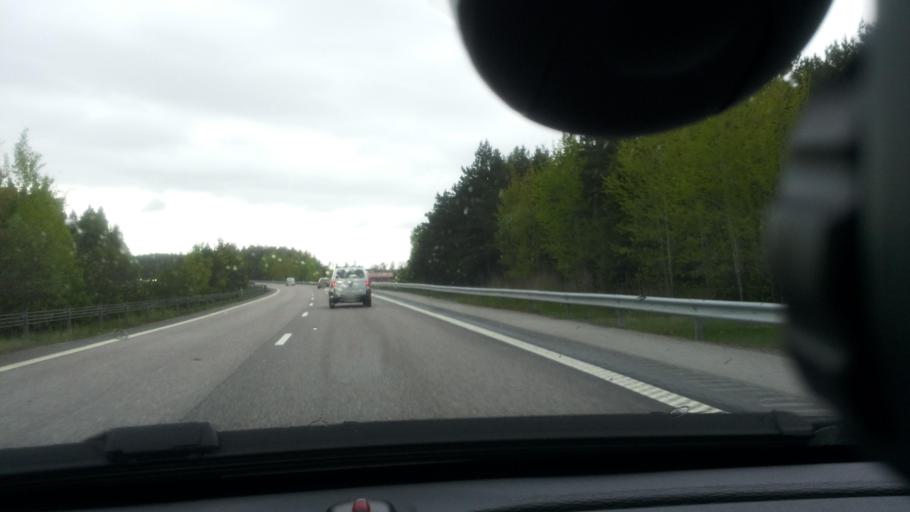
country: SE
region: Uppsala
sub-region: Knivsta Kommun
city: Knivsta
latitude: 59.7130
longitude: 17.8488
